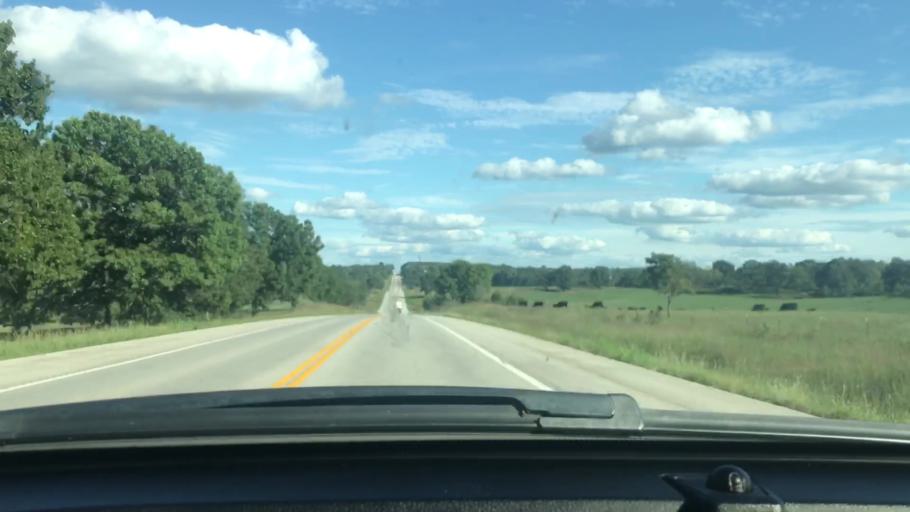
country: US
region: Missouri
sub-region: Howell County
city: West Plains
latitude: 36.6595
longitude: -91.7064
